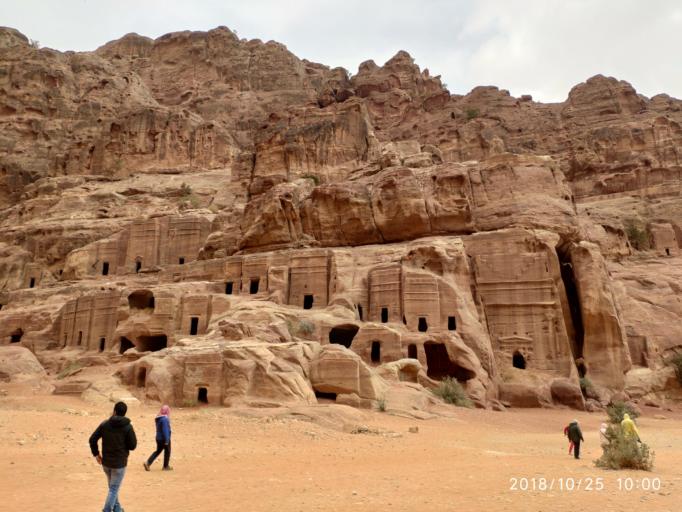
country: JO
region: Ma'an
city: Petra
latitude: 30.3241
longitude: 35.4486
